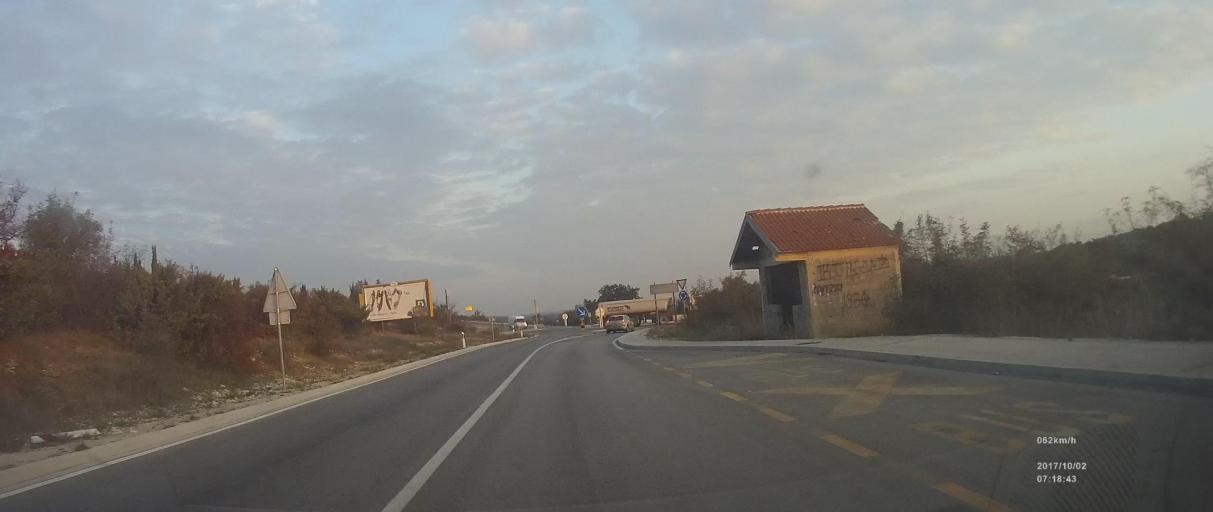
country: HR
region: Zadarska
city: Benkovac
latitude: 44.0201
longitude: 15.5917
